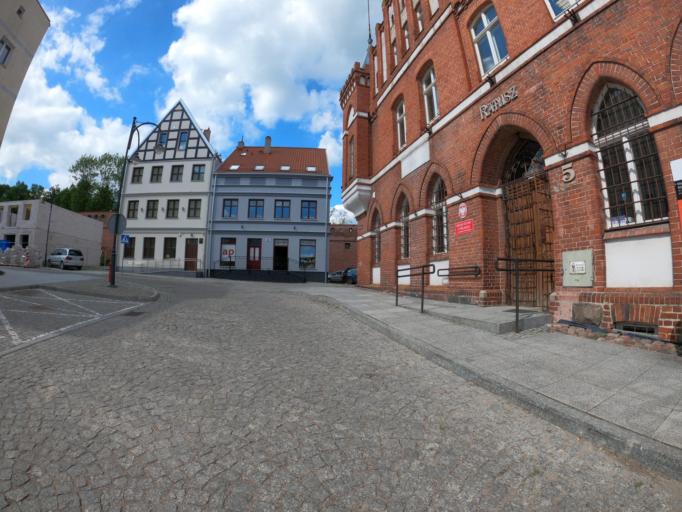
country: PL
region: Warmian-Masurian Voivodeship
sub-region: Powiat lidzbarski
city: Lidzbark Warminski
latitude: 54.1266
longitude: 20.5807
